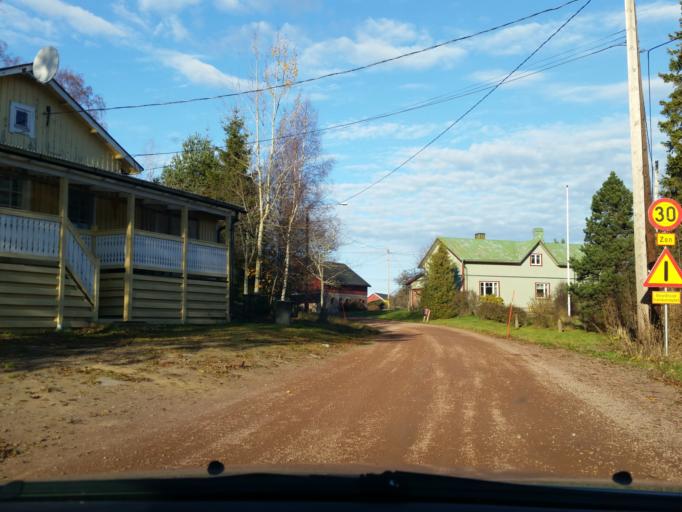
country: AX
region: Alands skaergard
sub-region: Braendoe
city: Braendoe
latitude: 60.4596
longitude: 21.0720
